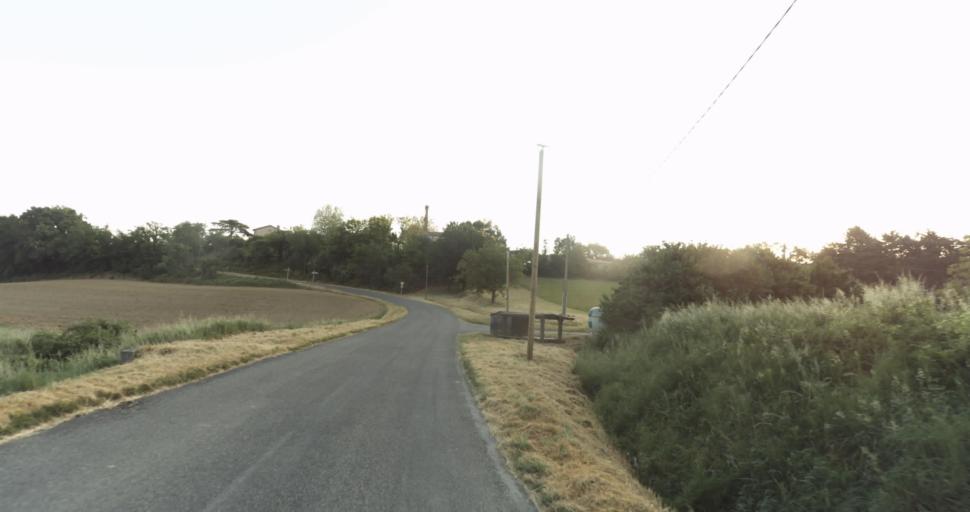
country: FR
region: Midi-Pyrenees
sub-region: Departement du Gers
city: Pujaudran
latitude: 43.6263
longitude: 1.1563
